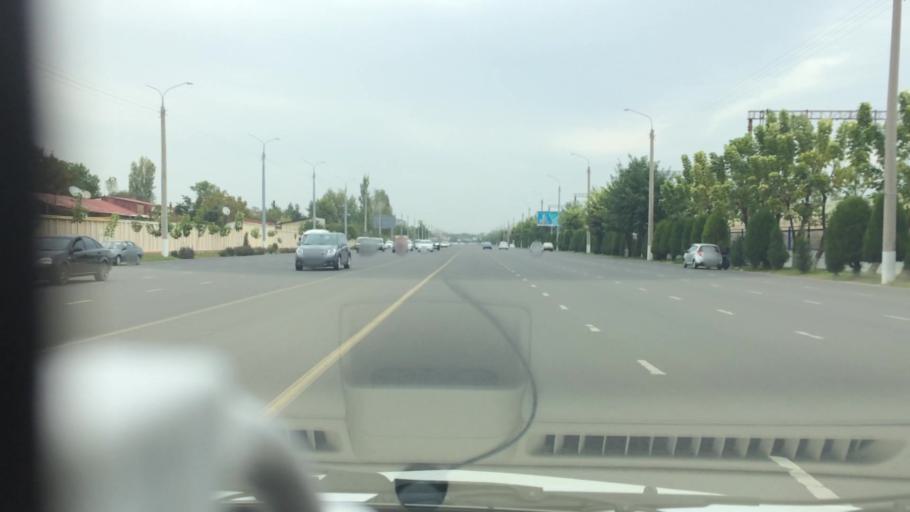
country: UZ
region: Toshkent Shahri
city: Tashkent
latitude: 41.2798
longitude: 69.2742
